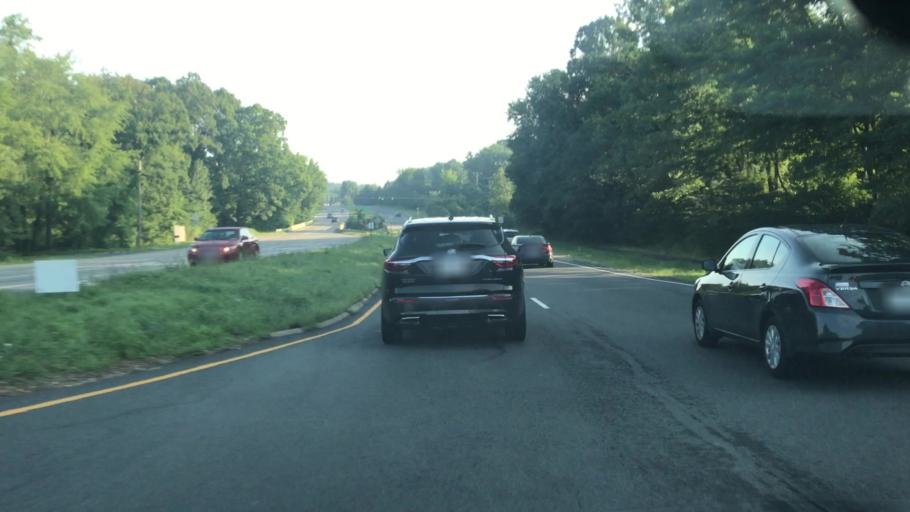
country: US
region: Virginia
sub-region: Fairfax County
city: Fairfax Station
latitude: 38.7990
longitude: -77.3253
